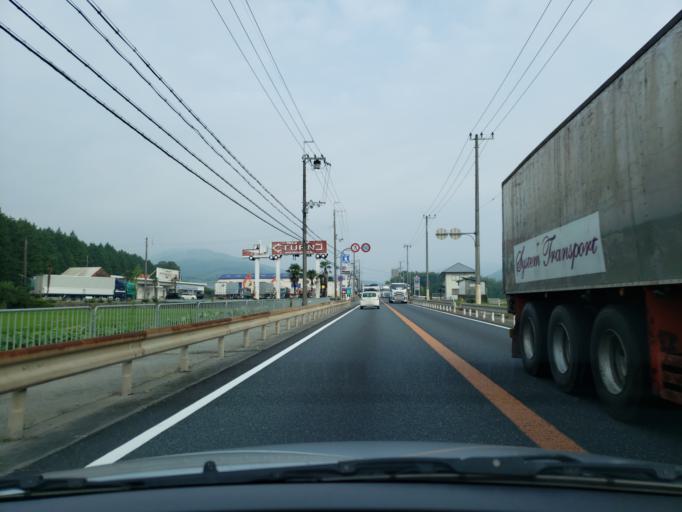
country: JP
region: Hyogo
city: Kariya
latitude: 34.8311
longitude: 134.3554
